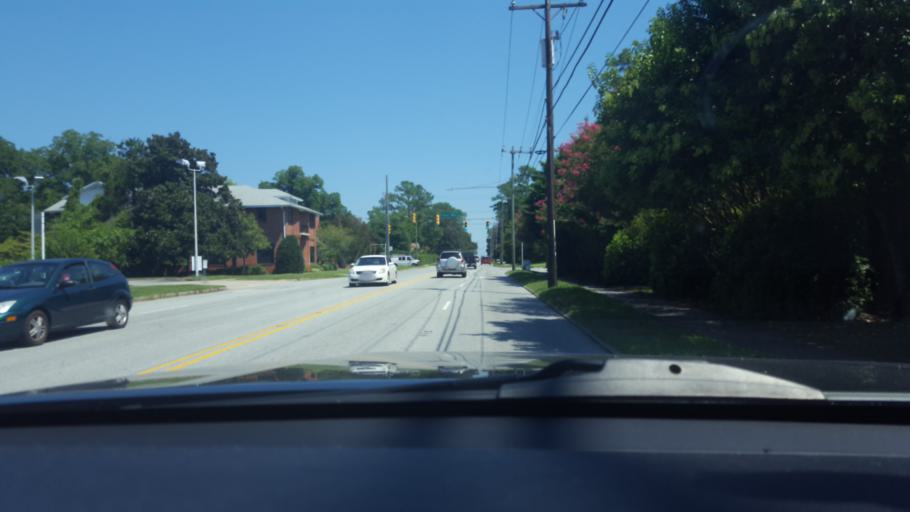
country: US
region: North Carolina
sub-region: New Hanover County
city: Wilmington
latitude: 34.2384
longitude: -77.9161
